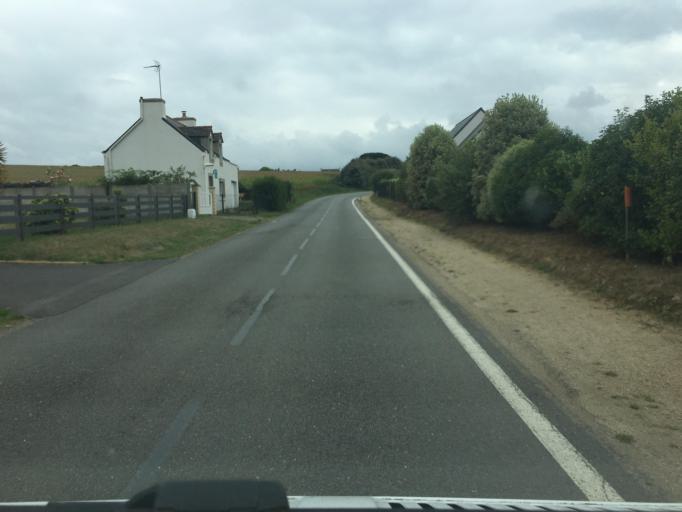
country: FR
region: Brittany
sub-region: Departement du Finistere
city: Plonevez-Porzay
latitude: 48.1346
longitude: -4.2590
